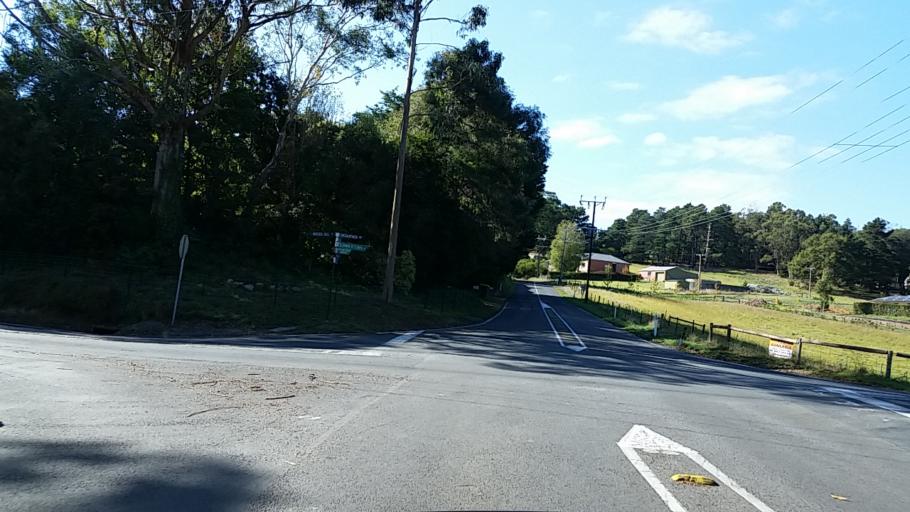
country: AU
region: South Australia
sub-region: Adelaide Hills
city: Adelaide Hills
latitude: -34.9434
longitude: 138.7293
